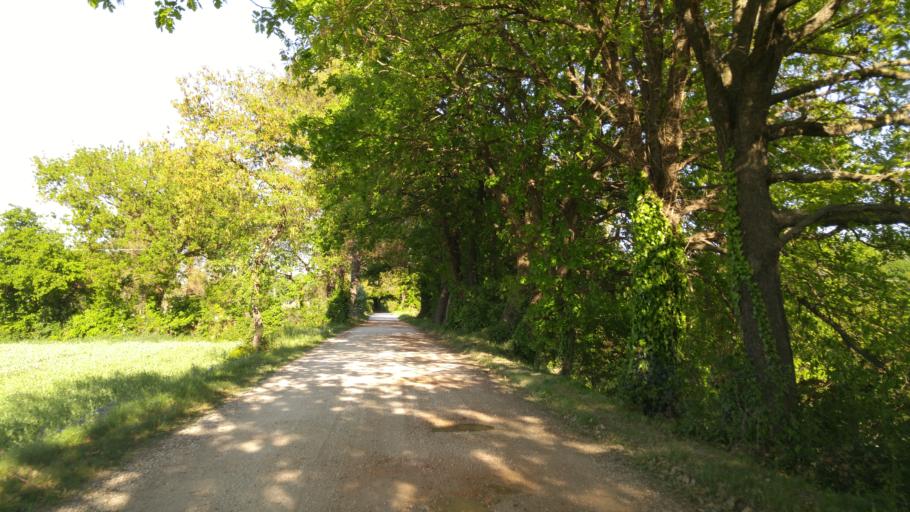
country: IT
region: The Marches
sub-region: Provincia di Pesaro e Urbino
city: Piagge
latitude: 43.7573
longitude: 12.9619
